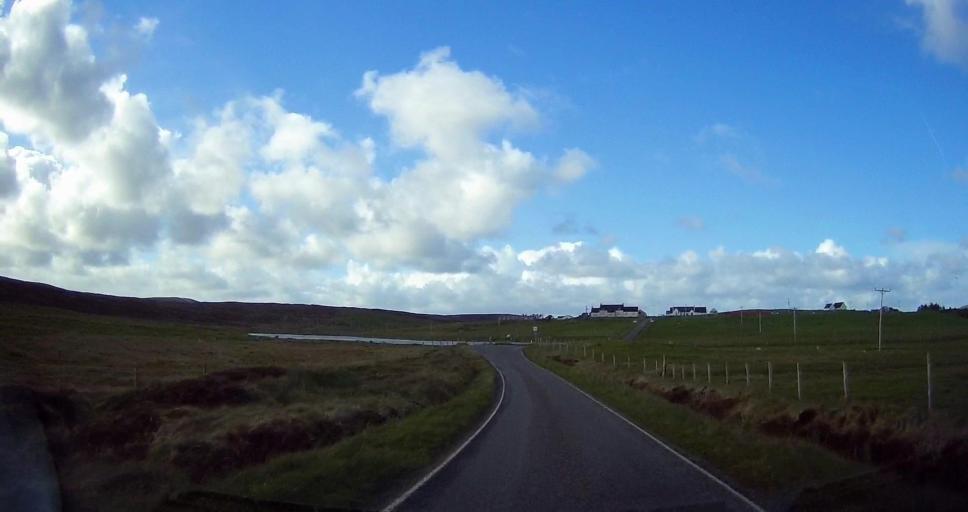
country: GB
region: Scotland
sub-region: Shetland Islands
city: Shetland
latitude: 60.3650
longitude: -1.1417
